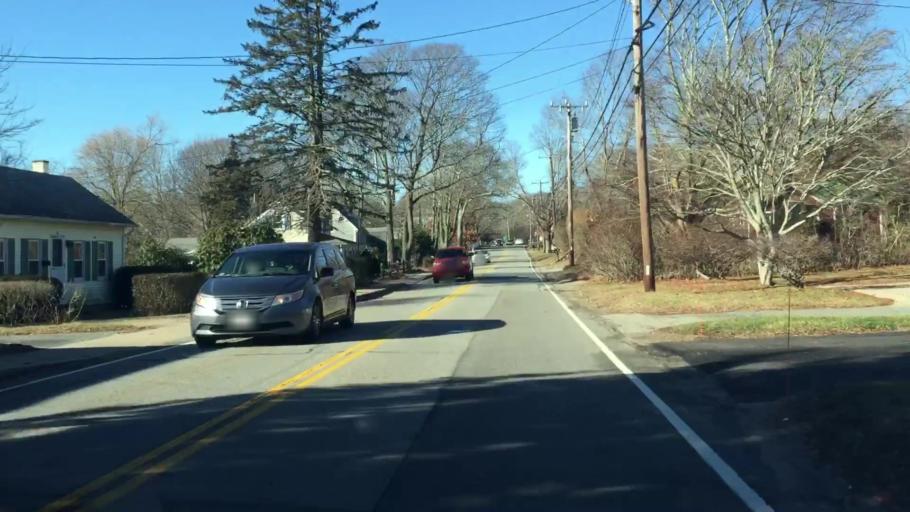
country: US
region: Massachusetts
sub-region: Barnstable County
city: Falmouth
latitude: 41.5630
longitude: -70.6154
